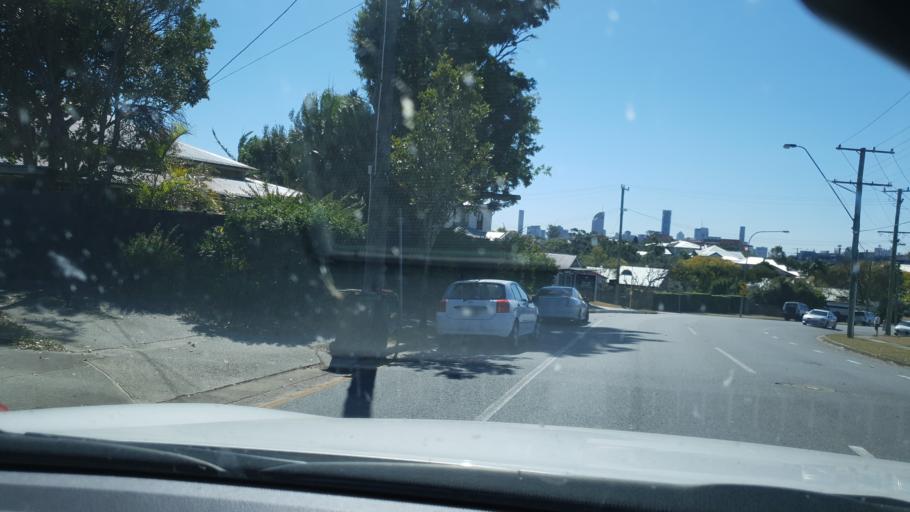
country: AU
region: Queensland
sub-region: Brisbane
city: Annerley
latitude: -27.5071
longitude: 153.0319
